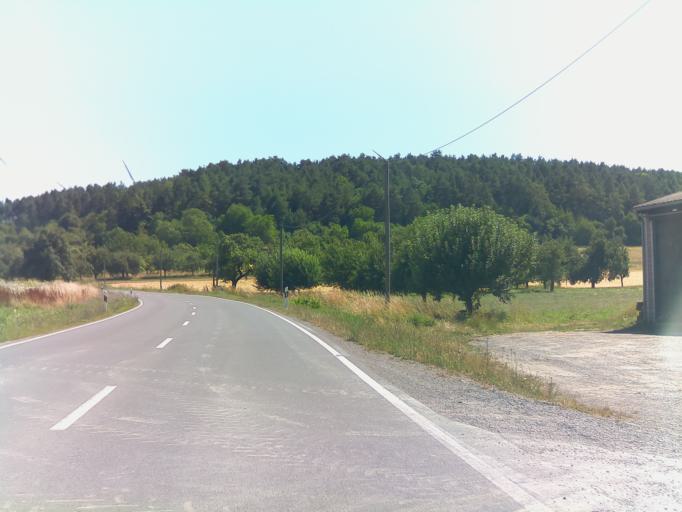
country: DE
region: Bavaria
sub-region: Regierungsbezirk Unterfranken
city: Helmstadt
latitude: 49.7585
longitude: 9.7066
